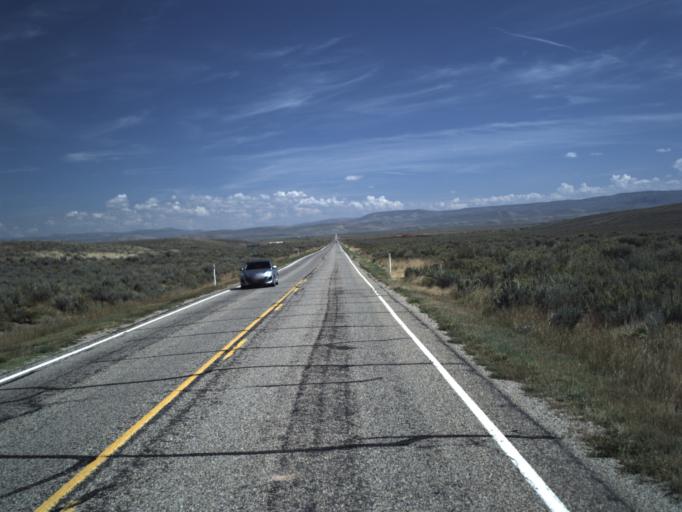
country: US
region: Utah
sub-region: Rich County
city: Randolph
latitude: 41.7699
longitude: -111.1499
